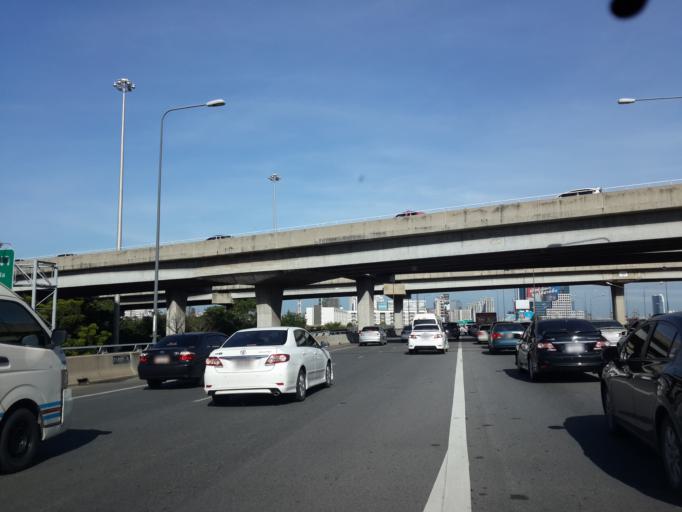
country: TH
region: Bangkok
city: Watthana
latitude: 13.7508
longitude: 100.5947
